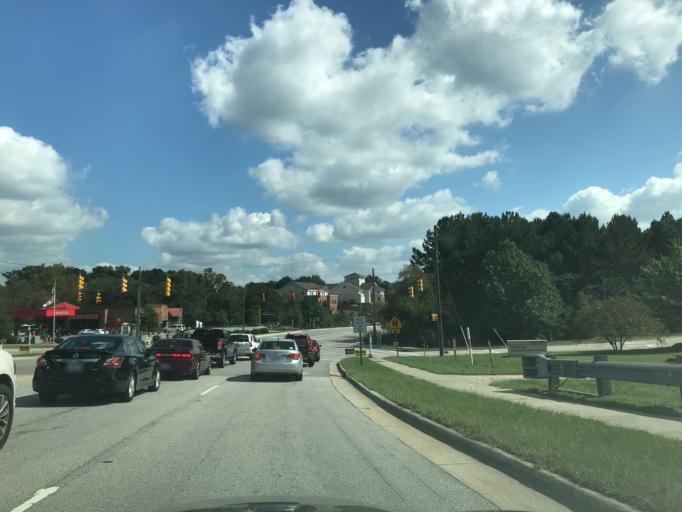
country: US
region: North Carolina
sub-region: Wake County
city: Wake Forest
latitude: 35.9502
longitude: -78.5104
